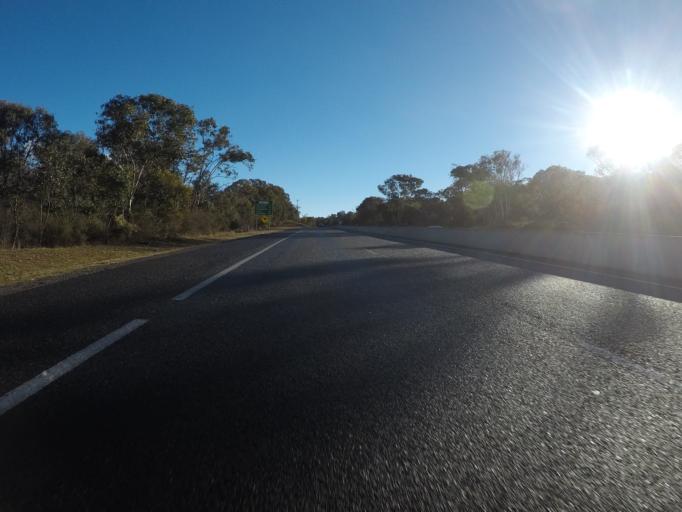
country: AU
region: Australian Capital Territory
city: Acton
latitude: -35.2763
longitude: 149.0870
